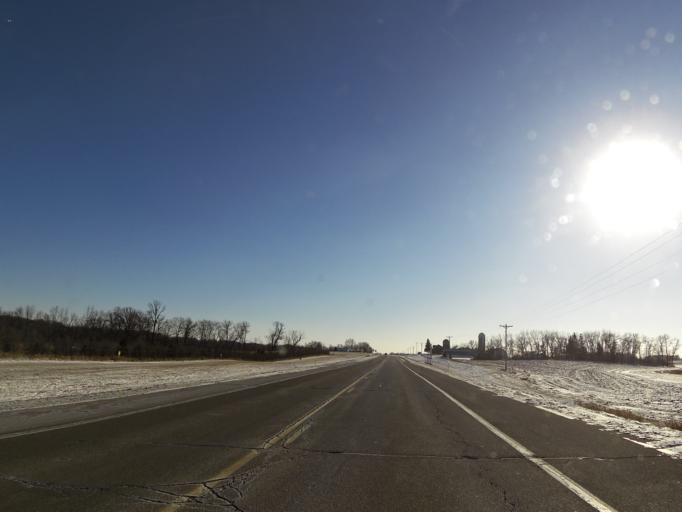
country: US
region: Minnesota
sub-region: Scott County
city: Prior Lake
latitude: 44.6859
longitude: -93.5010
